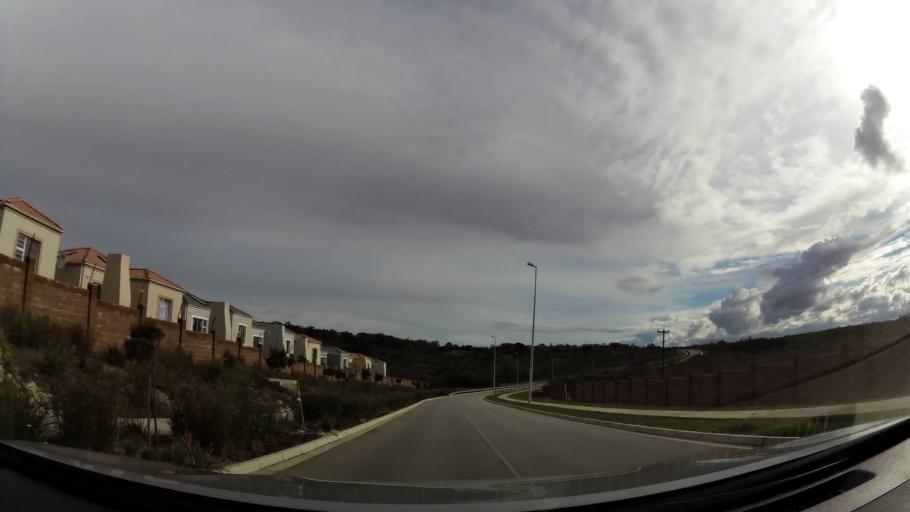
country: ZA
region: Eastern Cape
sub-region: Nelson Mandela Bay Metropolitan Municipality
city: Port Elizabeth
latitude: -33.9306
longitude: 25.4994
